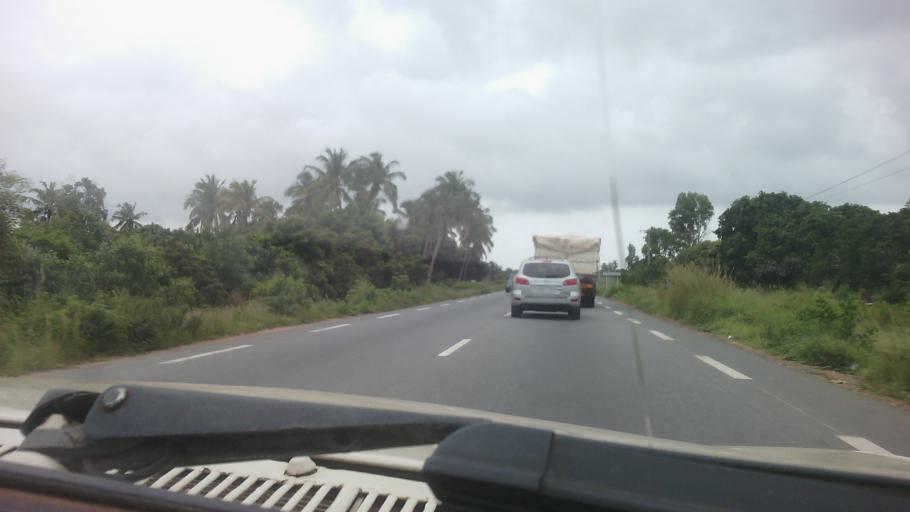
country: BJ
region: Atlantique
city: Ouidah
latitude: 6.3779
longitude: 2.0254
